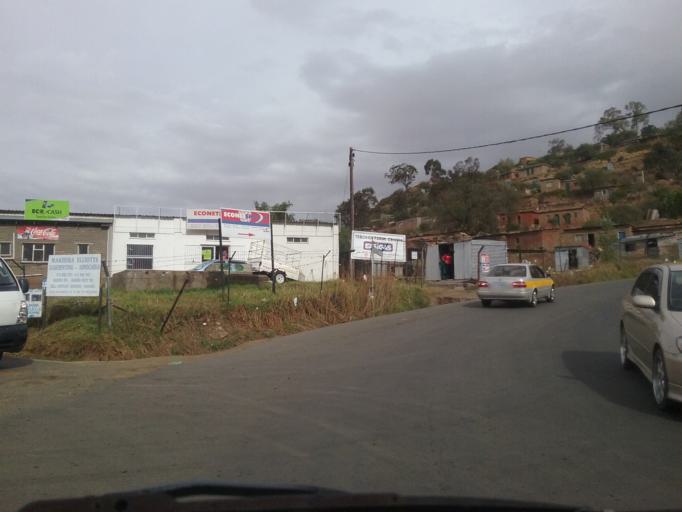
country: LS
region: Quthing
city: Quthing
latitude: -30.4005
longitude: 27.7044
